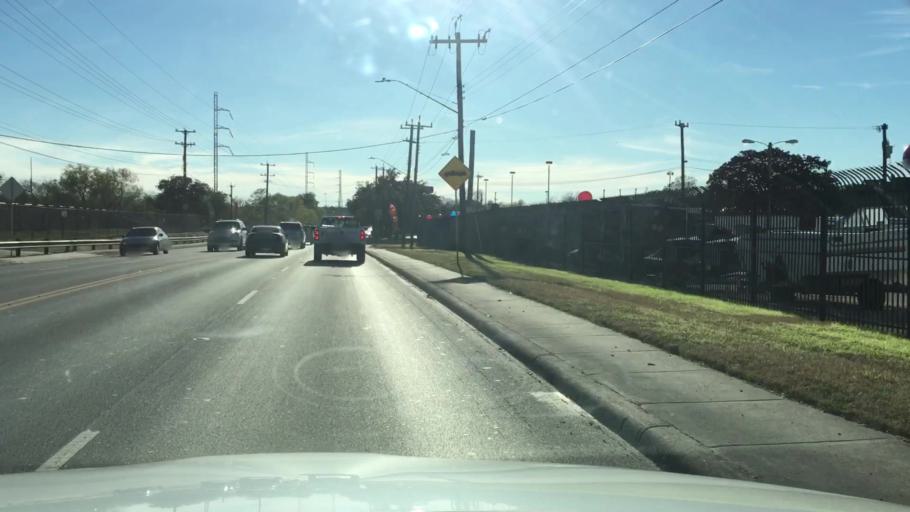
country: US
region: Texas
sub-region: Bexar County
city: Windcrest
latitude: 29.5387
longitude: -98.4234
